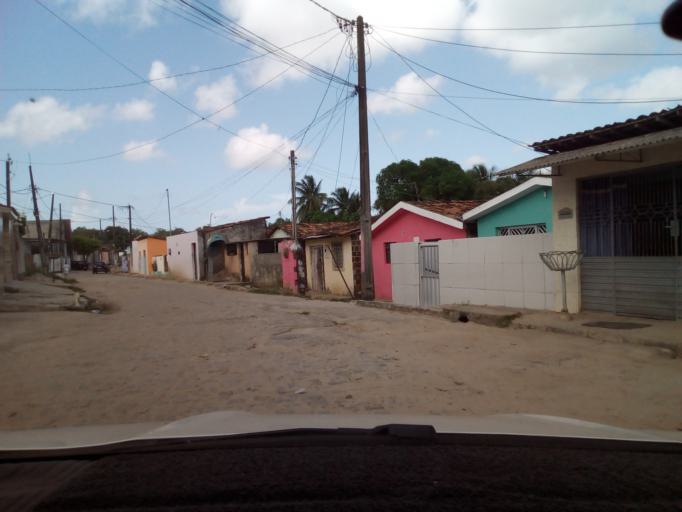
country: BR
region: Paraiba
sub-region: Bayeux
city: Bayeux
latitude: -7.1225
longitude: -34.9277
